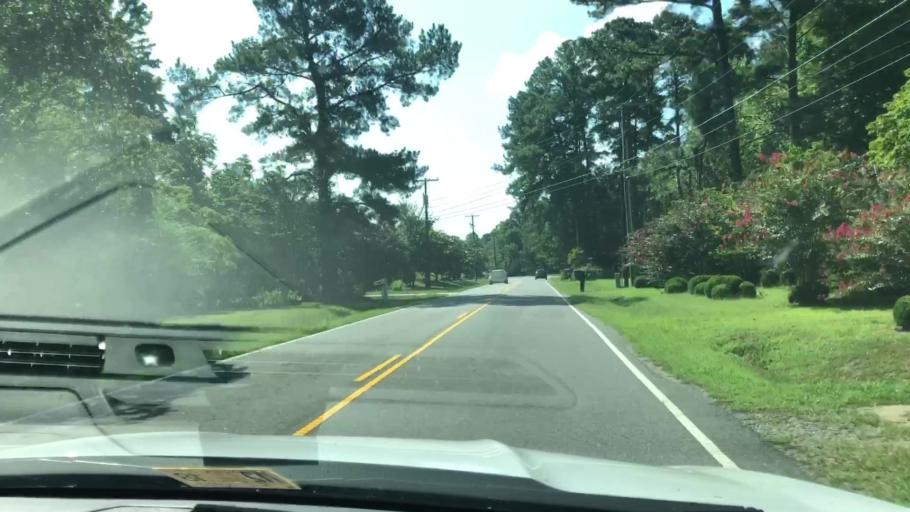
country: US
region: Virginia
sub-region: City of Poquoson
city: Poquoson
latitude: 37.1186
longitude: -76.4089
